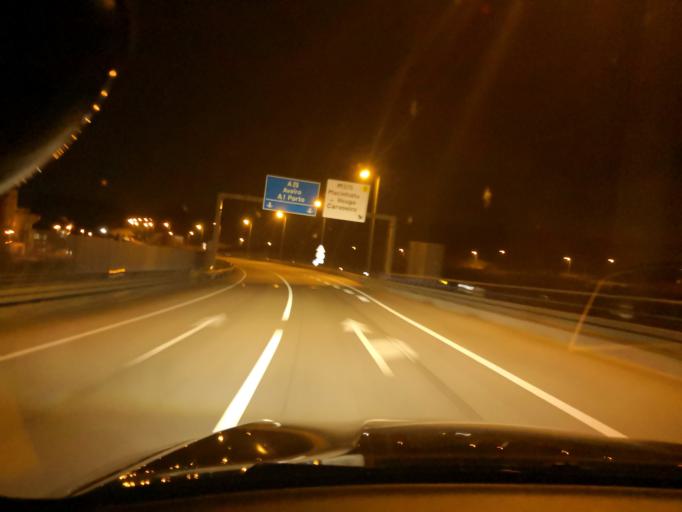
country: PT
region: Aveiro
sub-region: Albergaria-A-Velha
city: Albergaria-a-Velha
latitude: 40.6785
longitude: -8.4392
